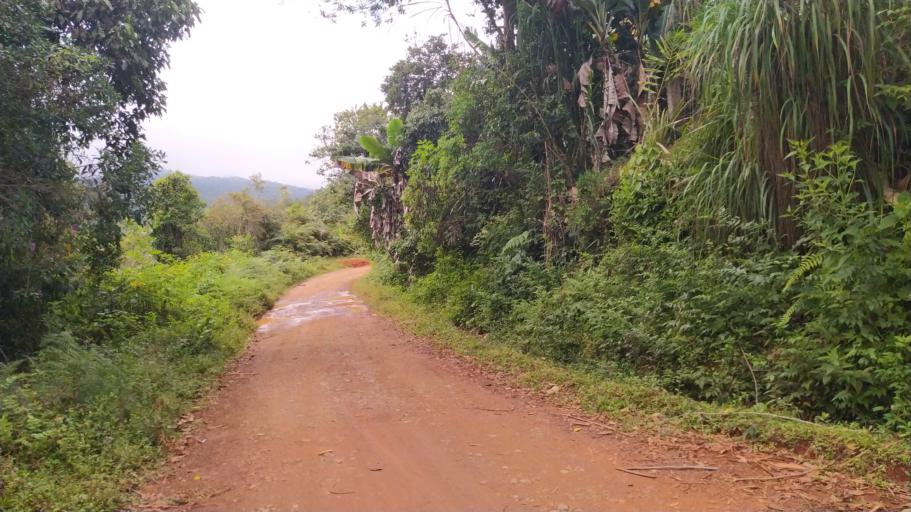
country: CO
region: Valle del Cauca
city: Cali
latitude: 3.4247
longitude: -76.6162
